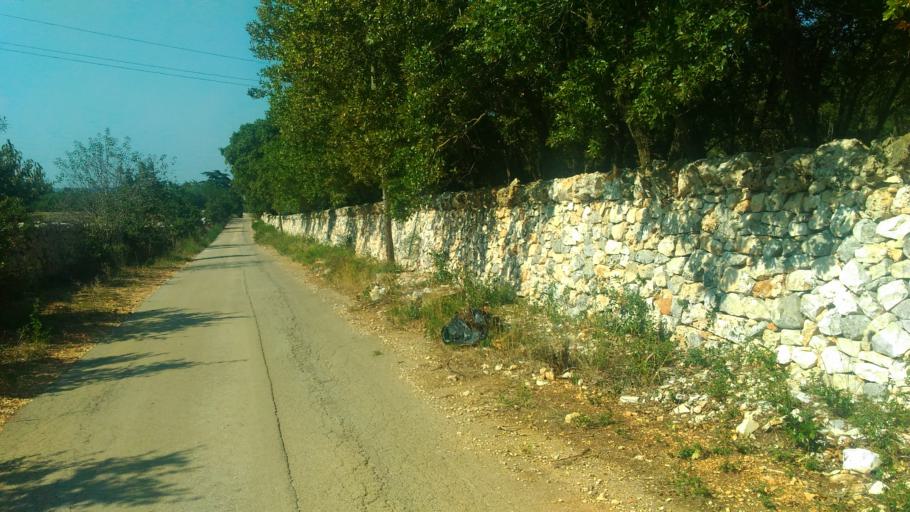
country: IT
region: Apulia
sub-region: Provincia di Bari
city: Noci
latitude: 40.8172
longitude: 17.1774
